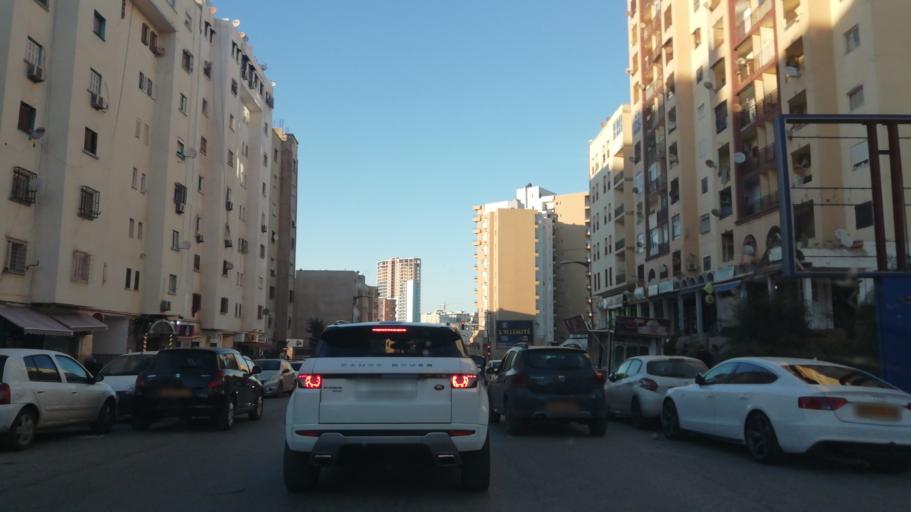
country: DZ
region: Oran
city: Bir el Djir
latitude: 35.7218
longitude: -0.5878
